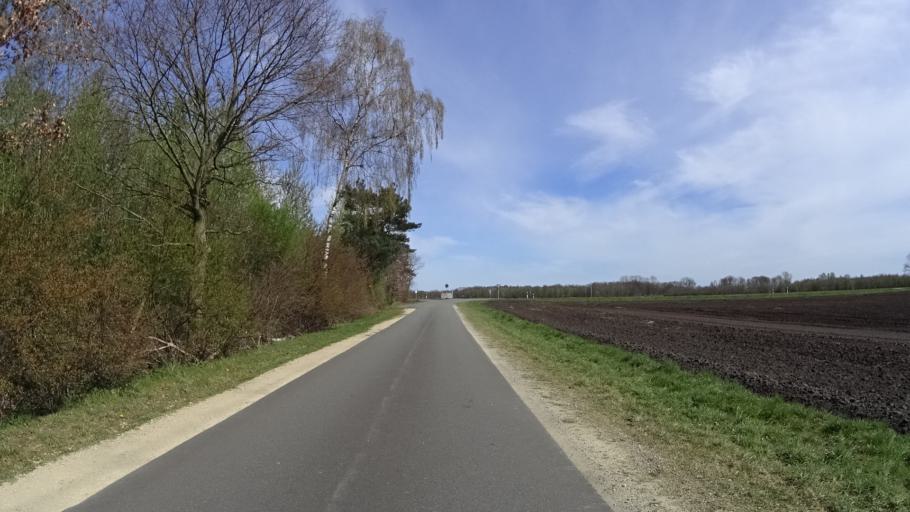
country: DE
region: Lower Saxony
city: Spelle
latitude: 52.3655
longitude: 7.4227
